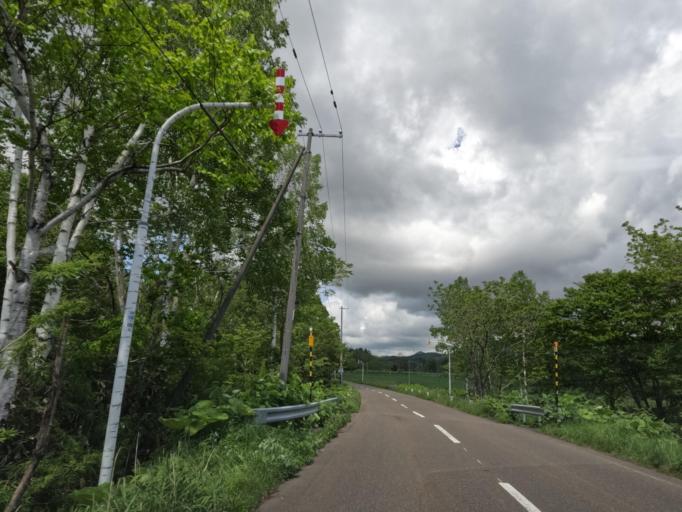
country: JP
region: Hokkaido
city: Tobetsu
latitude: 43.4518
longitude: 141.5900
